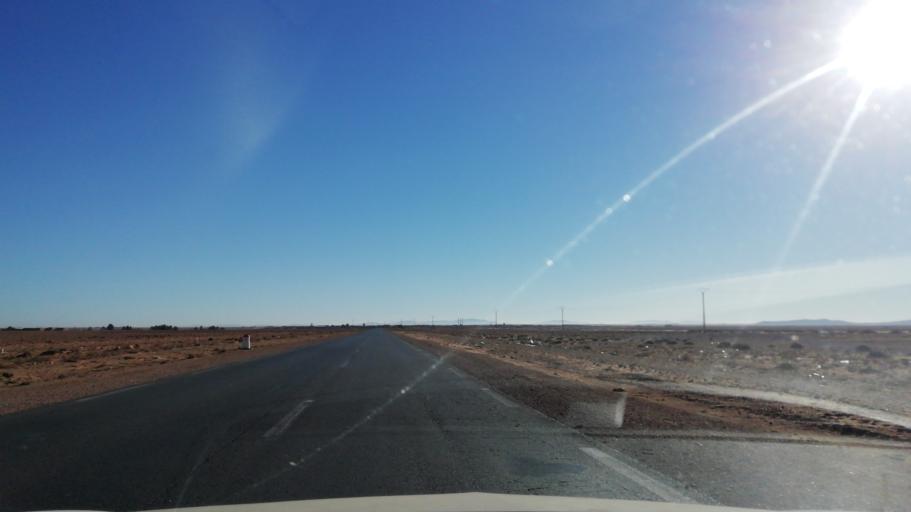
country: DZ
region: El Bayadh
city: El Bayadh
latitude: 33.8548
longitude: 0.6035
